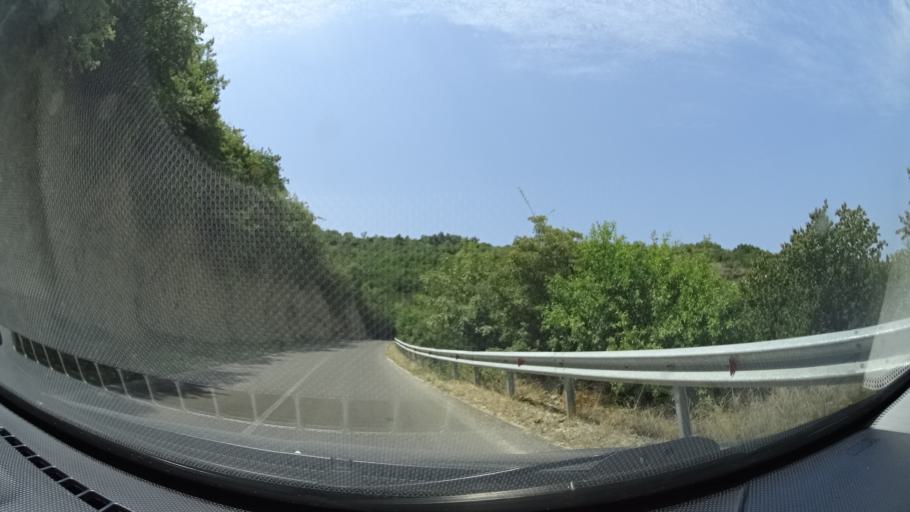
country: GE
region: Kakheti
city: Sighnaghi
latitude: 41.6226
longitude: 45.9325
